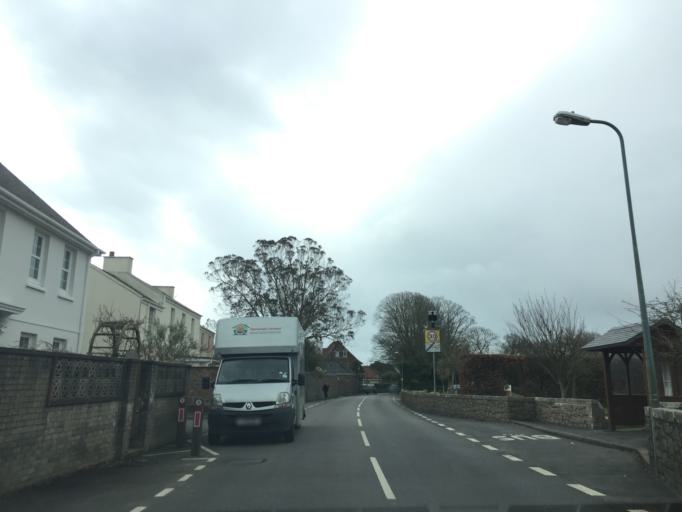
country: JE
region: St Helier
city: Saint Helier
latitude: 49.2140
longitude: -2.1412
